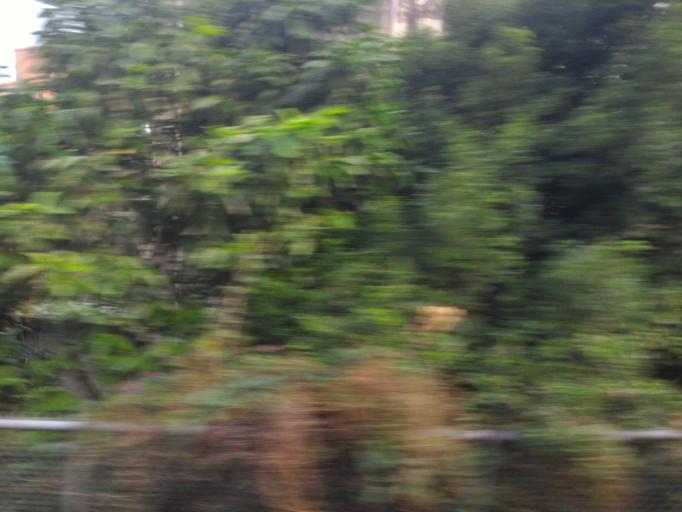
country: TW
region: Taiwan
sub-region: Taoyuan
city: Taoyuan
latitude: 24.9546
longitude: 121.3362
